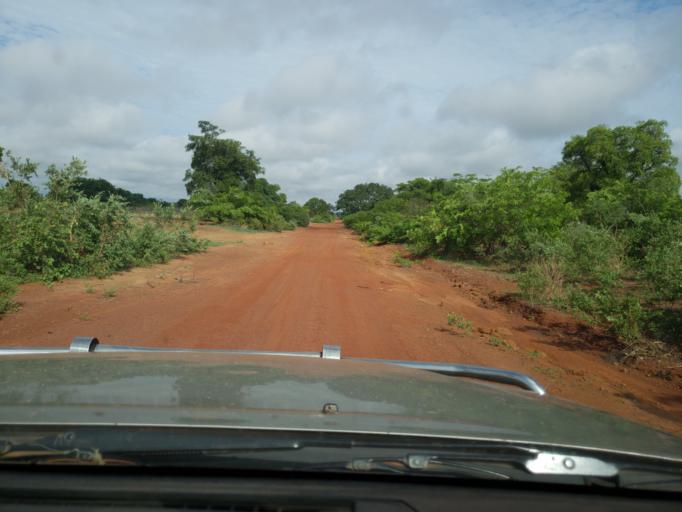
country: ML
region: Sikasso
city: Koutiala
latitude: 12.3924
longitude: -5.9997
